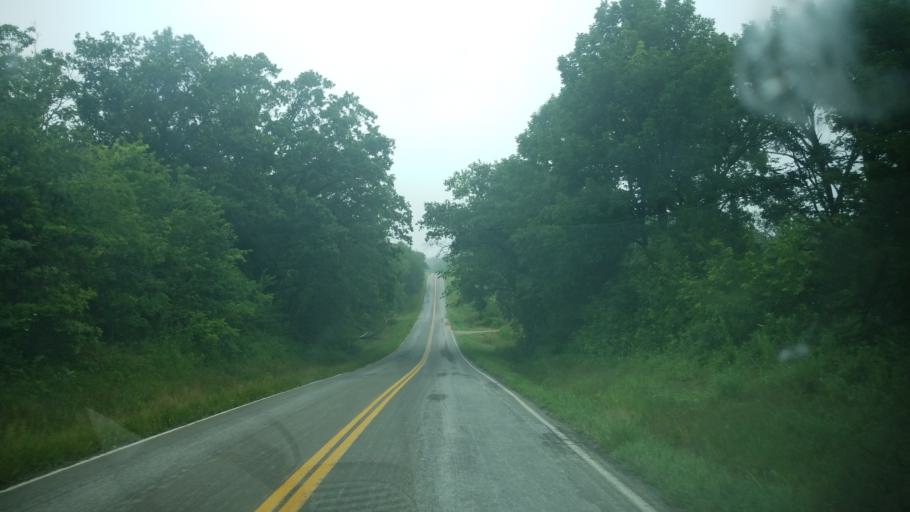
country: US
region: Missouri
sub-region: Audrain County
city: Vandalia
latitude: 39.3106
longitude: -91.3451
